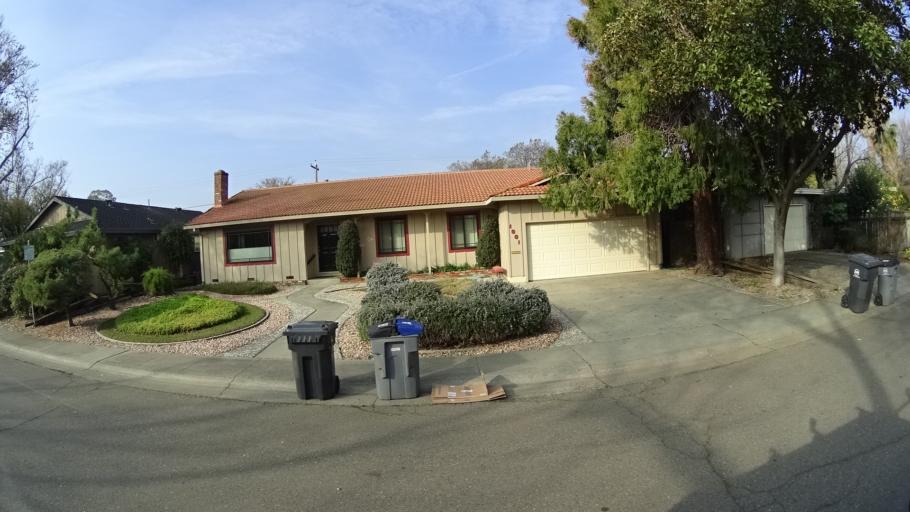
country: US
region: California
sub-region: Yolo County
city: Davis
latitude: 38.5521
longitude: -121.7660
